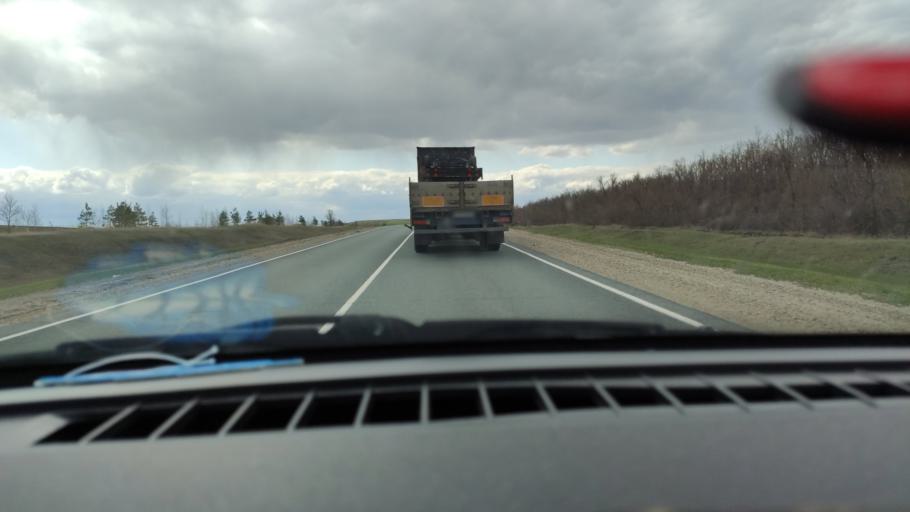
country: RU
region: Saratov
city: Alekseyevka
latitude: 52.2317
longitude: 47.9030
